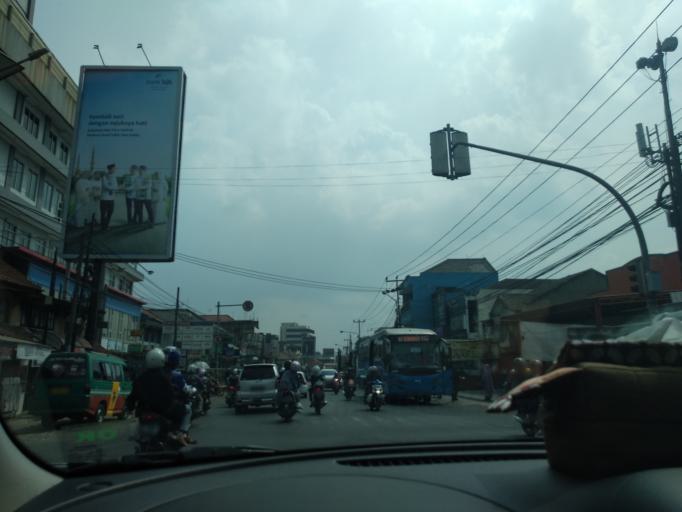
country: ID
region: West Java
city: Padalarang
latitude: -6.8633
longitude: 107.5035
